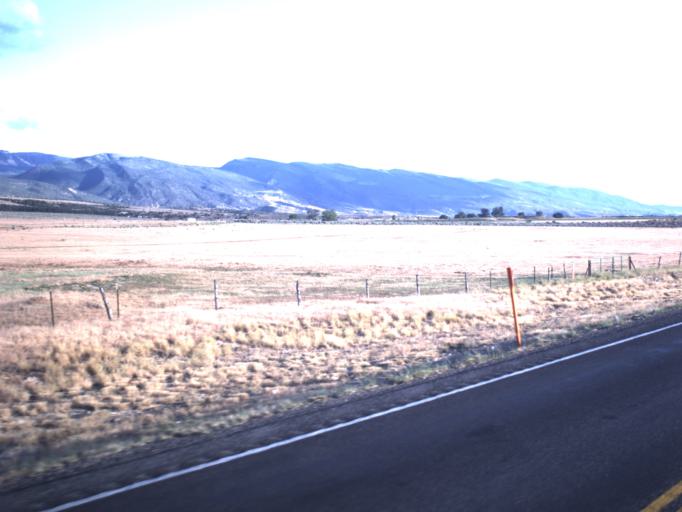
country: US
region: Utah
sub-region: Sanpete County
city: Ephraim
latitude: 39.4073
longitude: -111.5640
